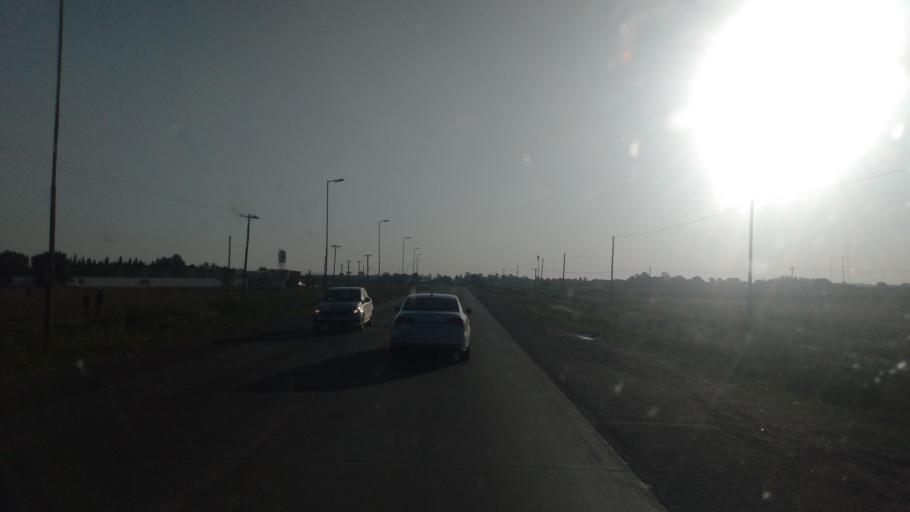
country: AR
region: Buenos Aires
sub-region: Partido de Campana
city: Campana
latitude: -34.1918
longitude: -58.9474
